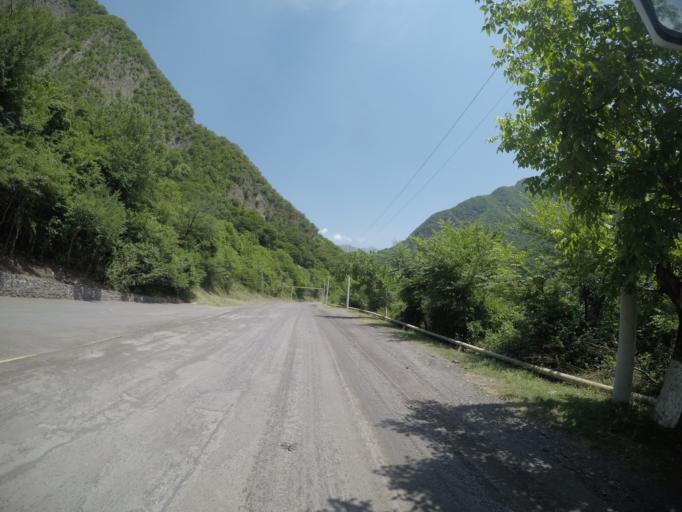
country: AZ
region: Qakh Rayon
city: Qaxbas
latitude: 41.4564
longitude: 47.0185
